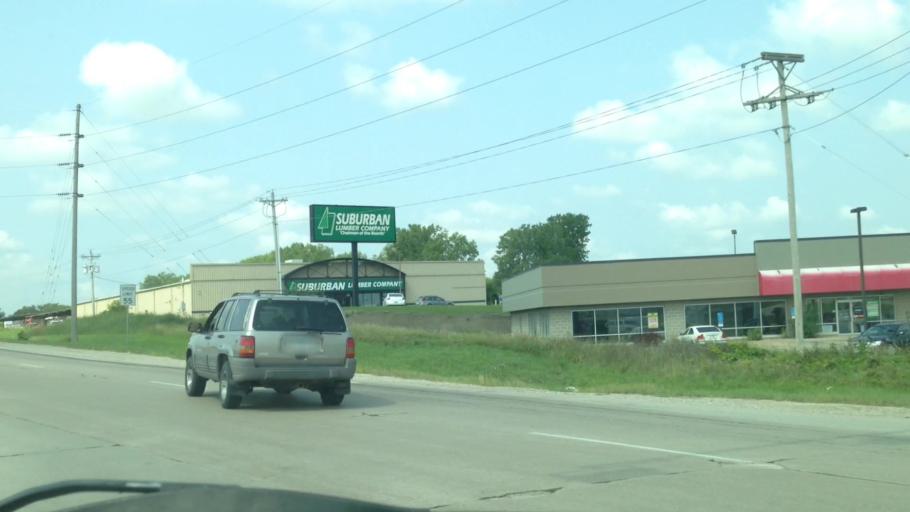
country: US
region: Iowa
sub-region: Linn County
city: Fairfax
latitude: 41.9520
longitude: -91.7249
